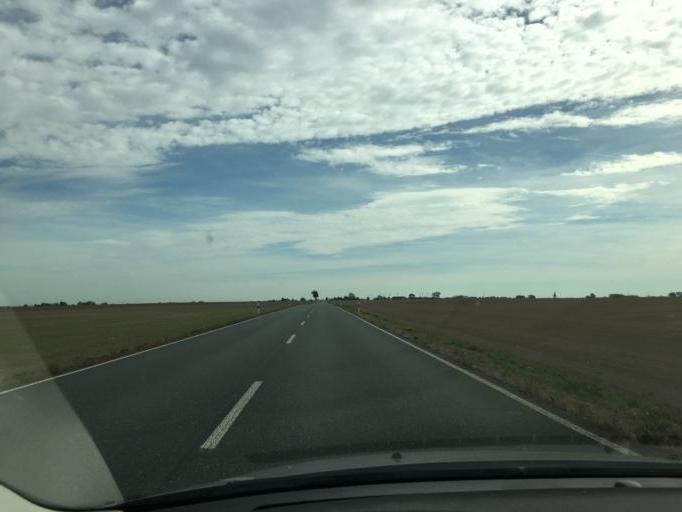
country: DE
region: Saxony
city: Riesa
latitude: 51.2586
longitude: 13.2715
